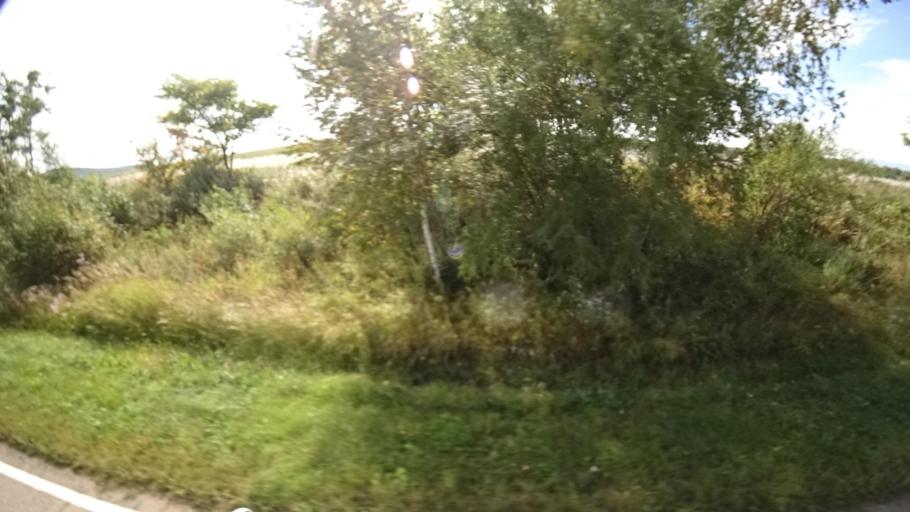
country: RU
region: Primorskiy
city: Yakovlevka
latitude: 44.4165
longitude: 133.5831
